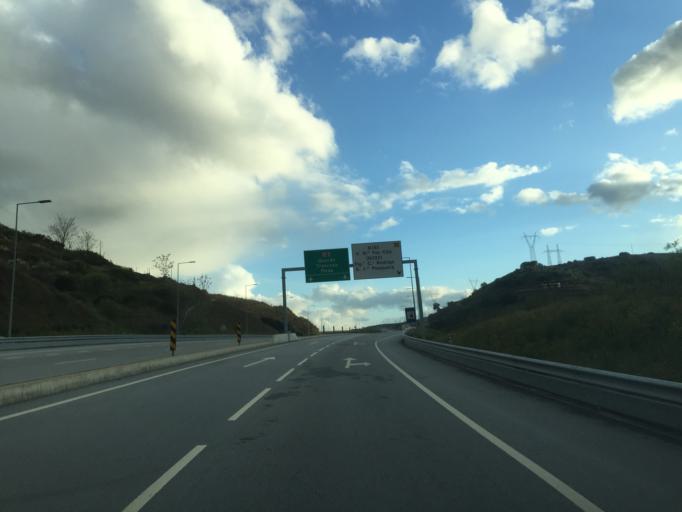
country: PT
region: Guarda
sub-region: Vila Nova de Foz Coa
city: Vila Nova de Foz Coa
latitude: 41.0595
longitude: -7.1658
